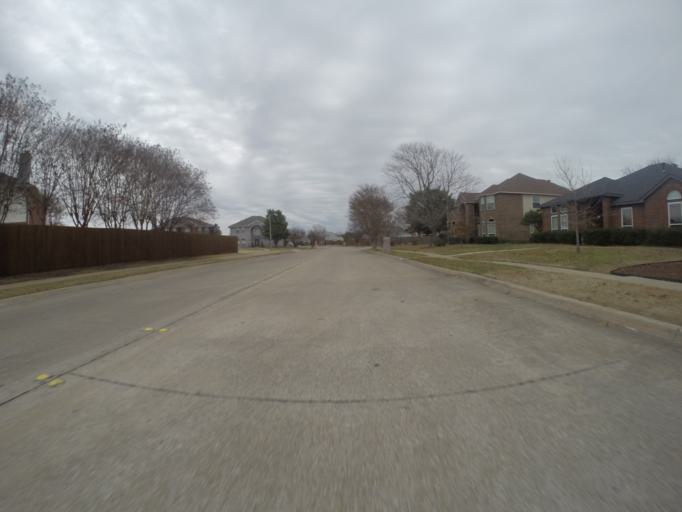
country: US
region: Texas
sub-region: Collin County
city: Saint Paul
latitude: 33.0429
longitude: -96.5604
